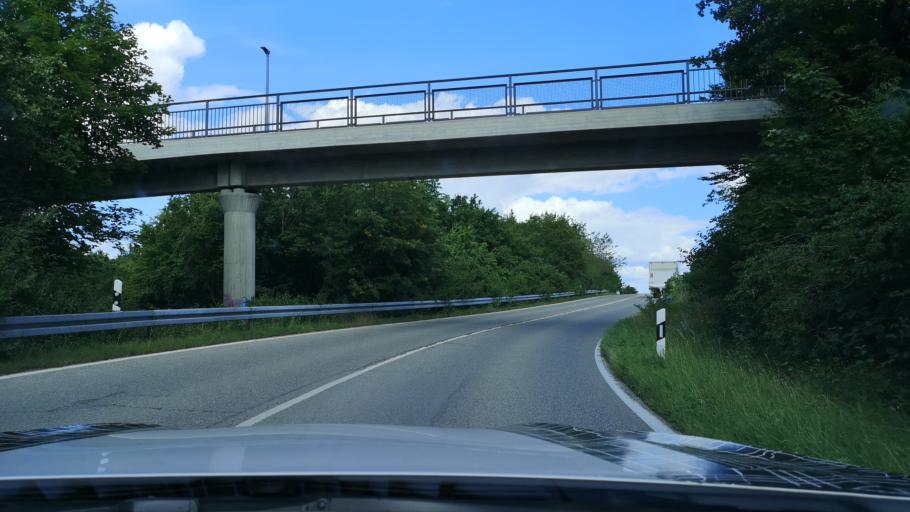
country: DE
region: Bavaria
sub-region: Upper Bavaria
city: Kirchheim bei Muenchen
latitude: 48.1715
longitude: 11.7528
